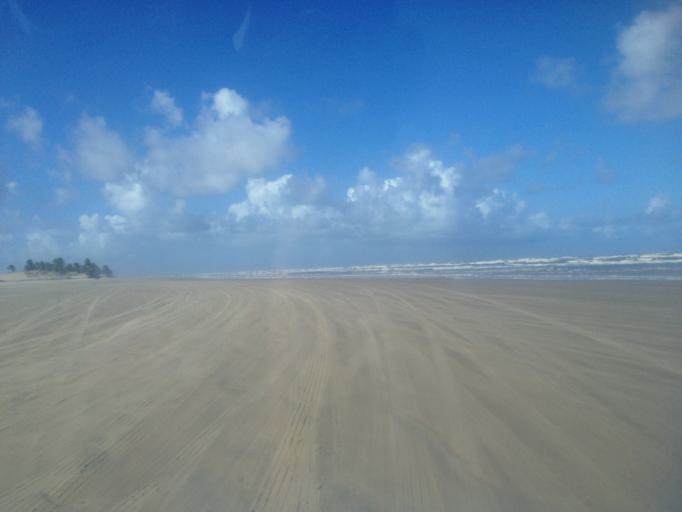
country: BR
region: Sergipe
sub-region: Indiaroba
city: Indiaroba
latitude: -11.4764
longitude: -37.3629
